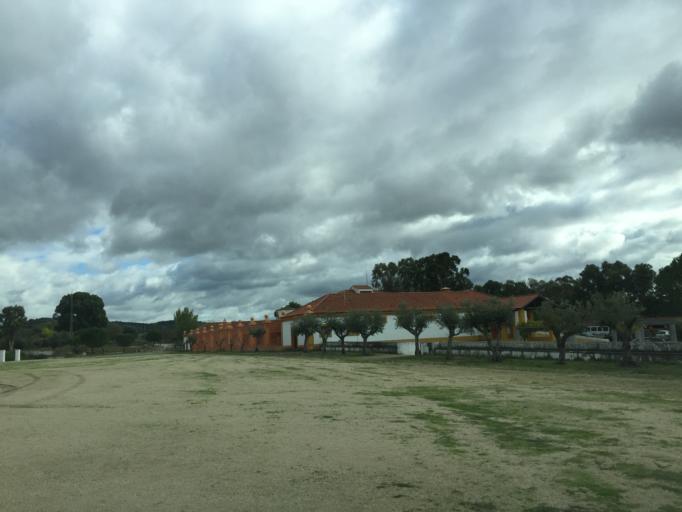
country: PT
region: Portalegre
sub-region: Alter do Chao
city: Alter do Chao
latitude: 39.2222
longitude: -7.6869
